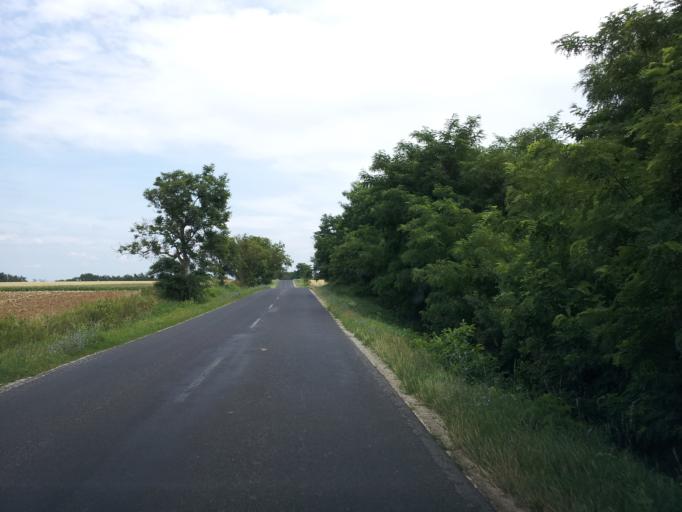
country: HU
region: Vas
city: Vasvar
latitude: 47.0276
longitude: 16.9264
